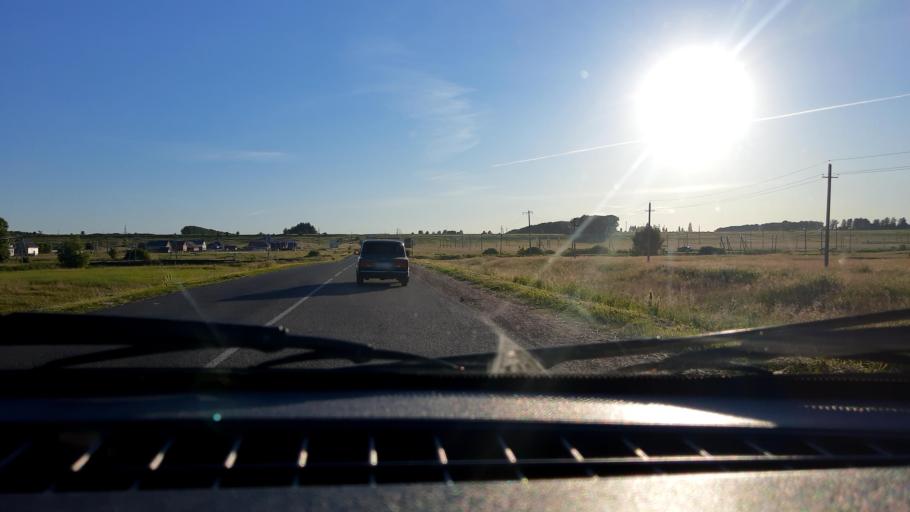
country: RU
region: Bashkortostan
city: Mikhaylovka
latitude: 54.8884
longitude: 55.8838
